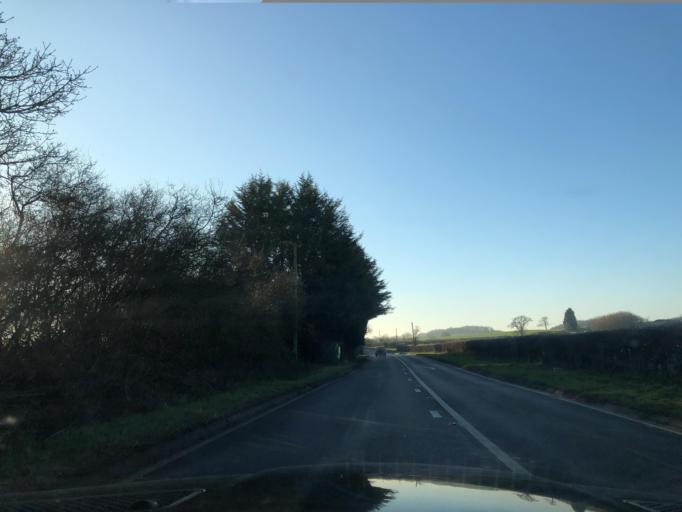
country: GB
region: England
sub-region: Warwickshire
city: Warwick
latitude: 52.2733
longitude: -1.6407
